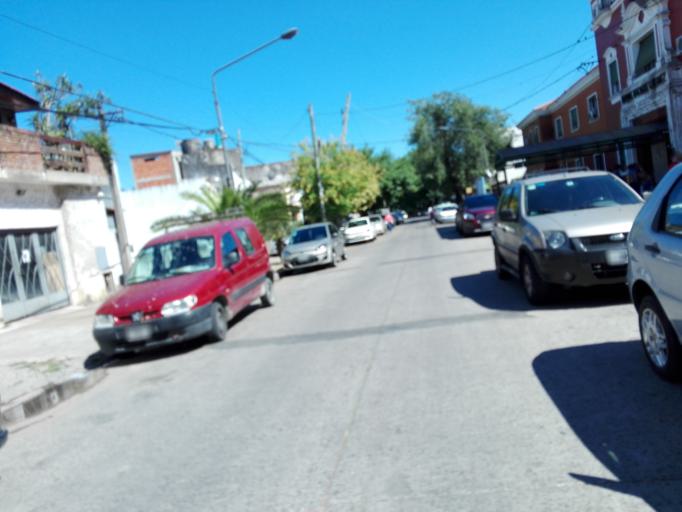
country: AR
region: Buenos Aires
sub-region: Partido de La Plata
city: La Plata
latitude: -34.8962
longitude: -57.9480
